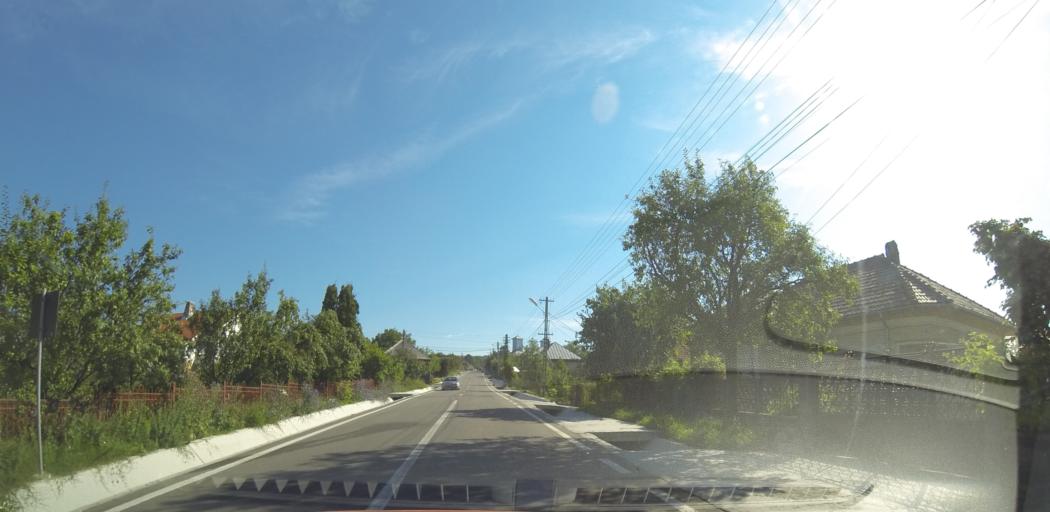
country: RO
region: Valcea
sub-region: Comuna Vaideeni
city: Vaideeni
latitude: 45.1651
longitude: 23.8976
